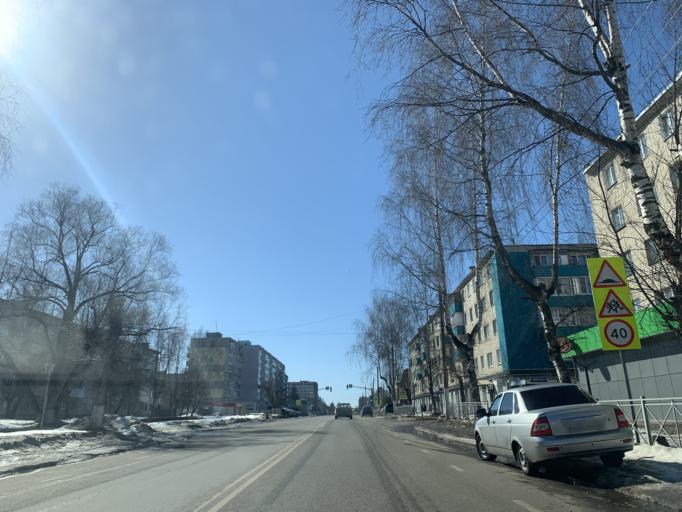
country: RU
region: Jaroslavl
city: Tutayev
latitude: 57.8689
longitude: 39.5125
